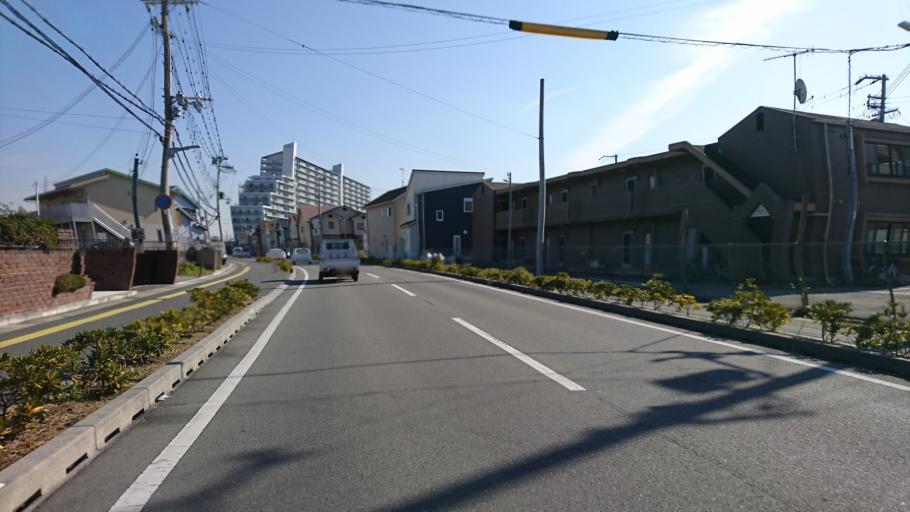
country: JP
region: Hyogo
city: Kakogawacho-honmachi
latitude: 34.7743
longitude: 134.8059
